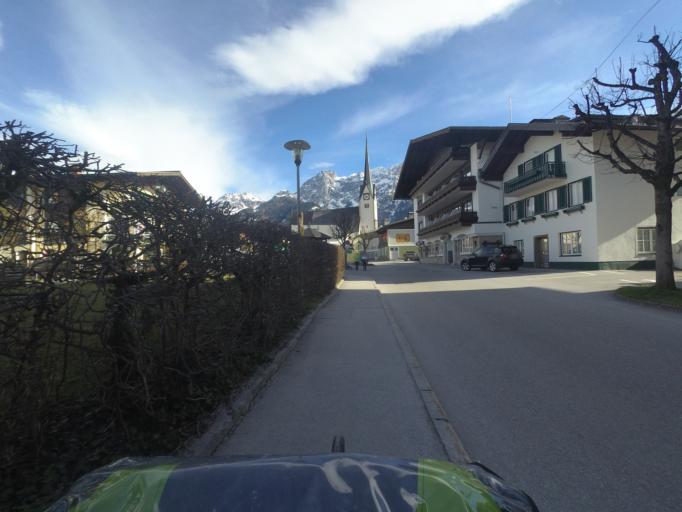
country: AT
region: Salzburg
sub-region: Politischer Bezirk Hallein
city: Abtenau
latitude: 47.5654
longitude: 13.3458
